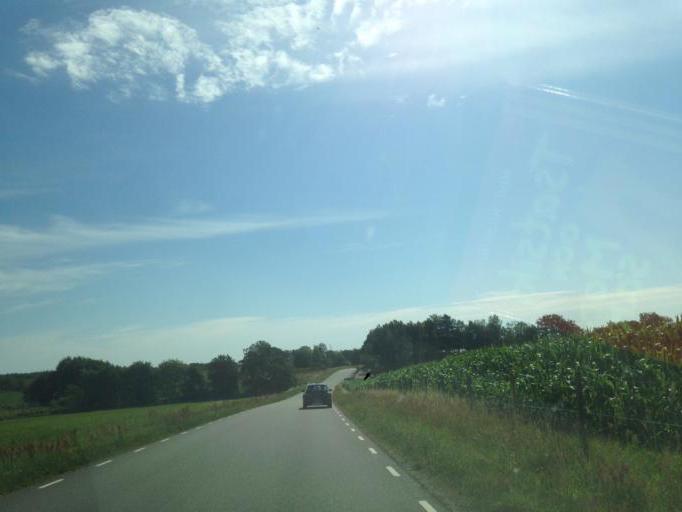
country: SE
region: Skane
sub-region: Simrishamns Kommun
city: Kivik
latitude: 55.6367
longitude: 14.1466
